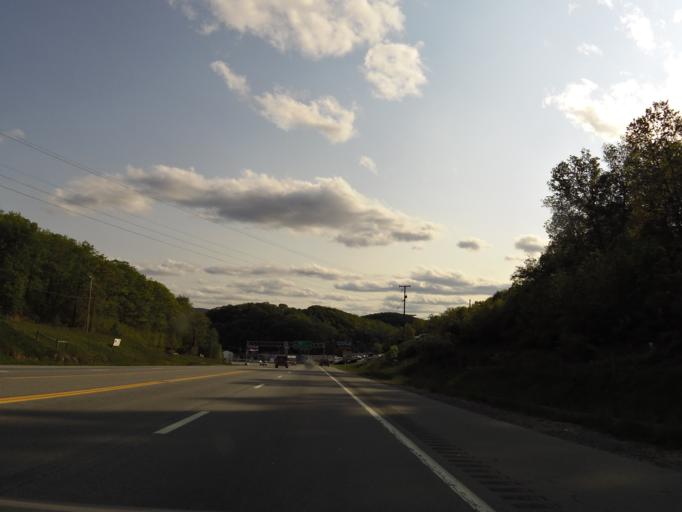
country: US
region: West Virginia
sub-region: Mercer County
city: Princeton
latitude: 37.3264
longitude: -81.1324
